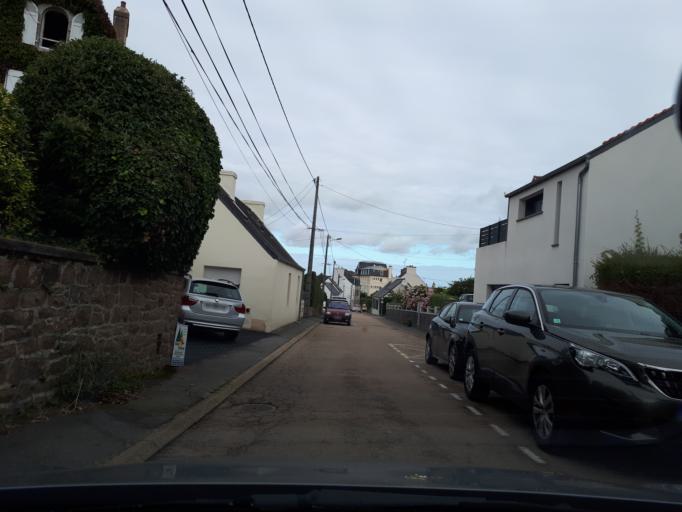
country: FR
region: Brittany
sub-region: Departement du Finistere
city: Carantec
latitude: 48.6697
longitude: -3.9192
